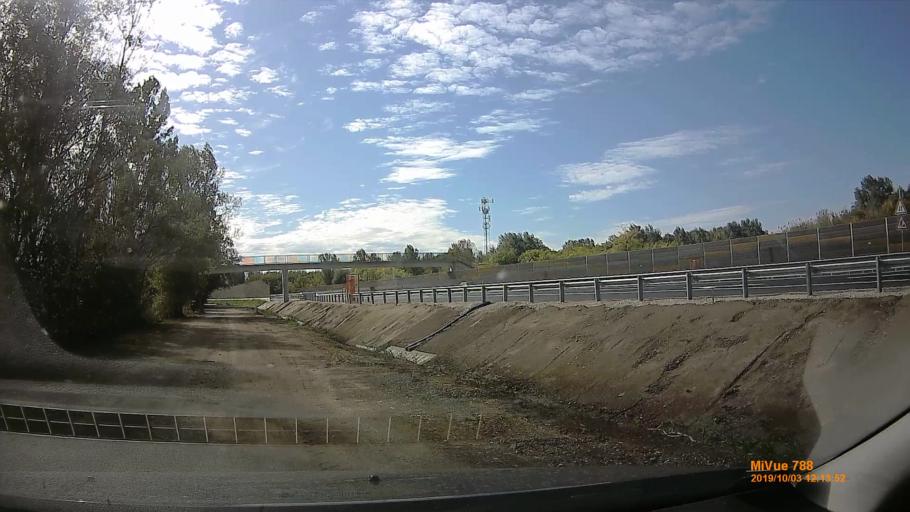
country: HU
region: Pest
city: Szodliget
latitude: 47.7280
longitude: 19.1583
